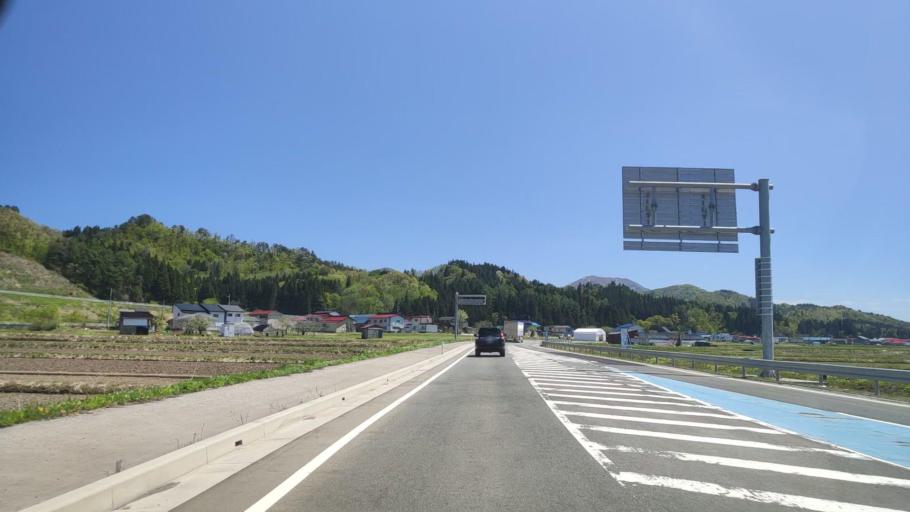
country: JP
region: Yamagata
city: Obanazawa
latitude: 38.5608
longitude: 140.3991
